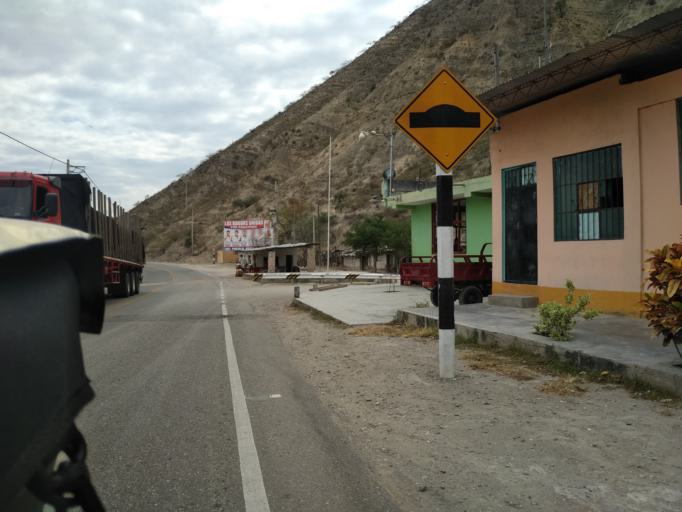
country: PE
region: Cajamarca
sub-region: Provincia de Jaen
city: Bellavista
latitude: -5.7537
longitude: -78.6904
